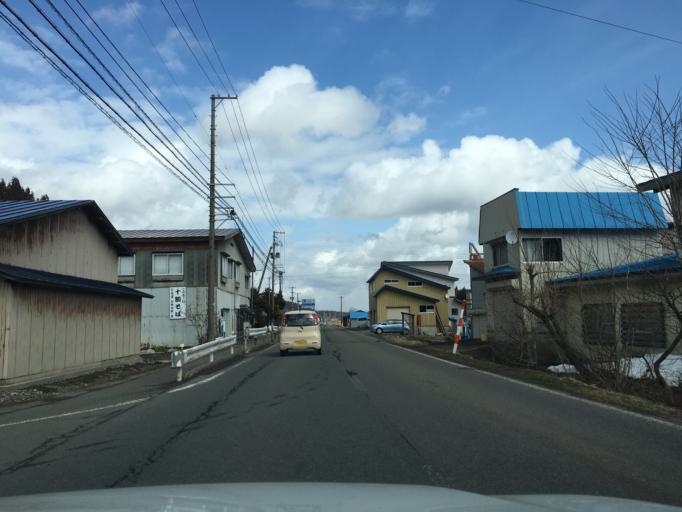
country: JP
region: Akita
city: Takanosu
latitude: 40.0343
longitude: 140.2754
